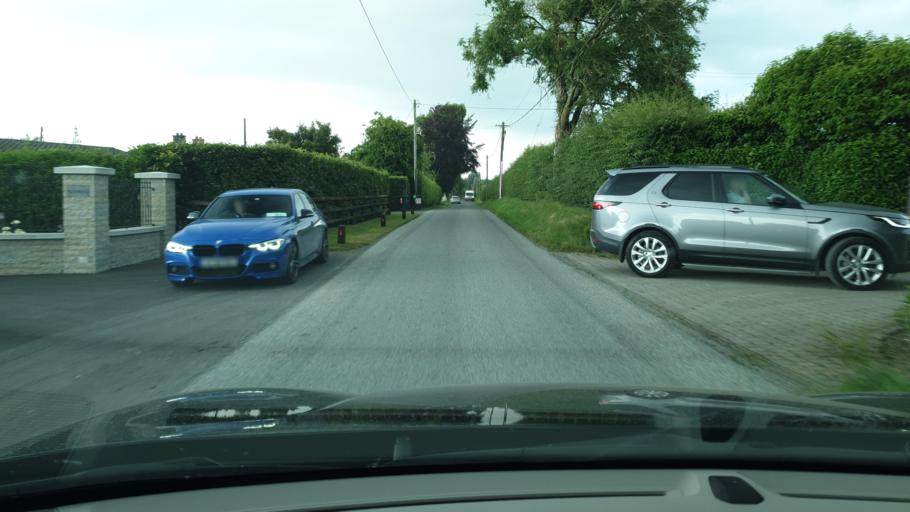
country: IE
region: Leinster
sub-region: An Mhi
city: Dunshaughlin
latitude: 53.4983
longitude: -6.5134
